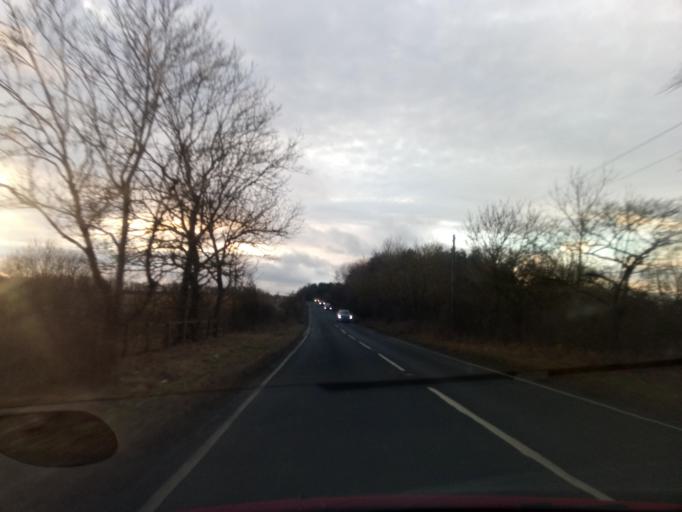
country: GB
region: England
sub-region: Newcastle upon Tyne
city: Dinnington
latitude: 55.0752
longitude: -1.6789
